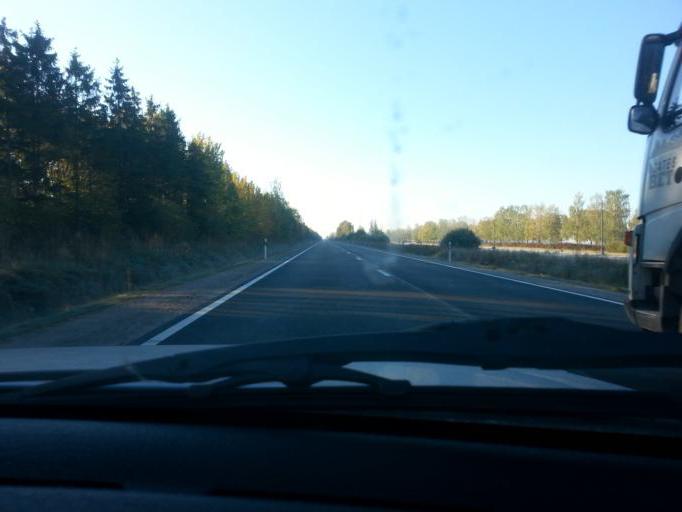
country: LV
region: Jelgava
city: Jelgava
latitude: 56.5026
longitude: 23.7003
